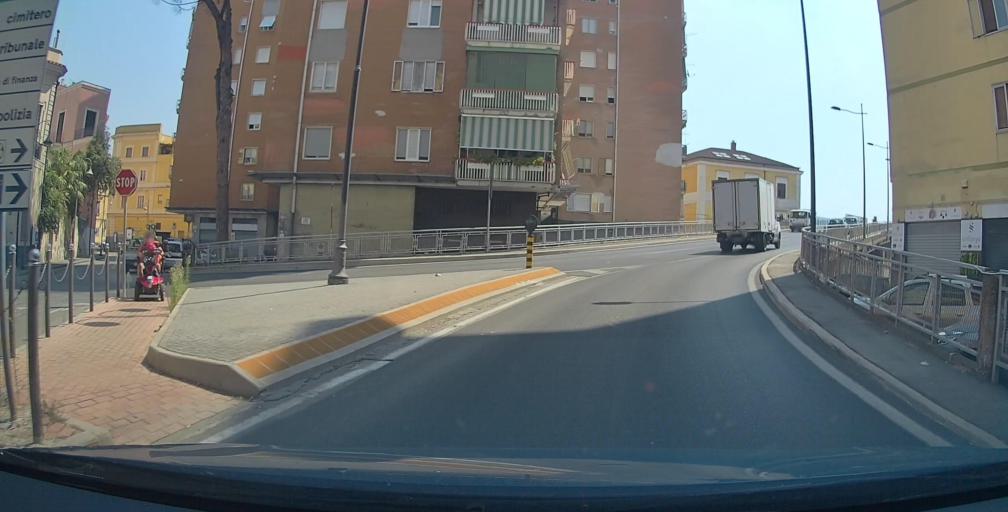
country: IT
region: Campania
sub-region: Provincia di Salerno
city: Nocera Inferiore
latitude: 40.7450
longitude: 14.6470
